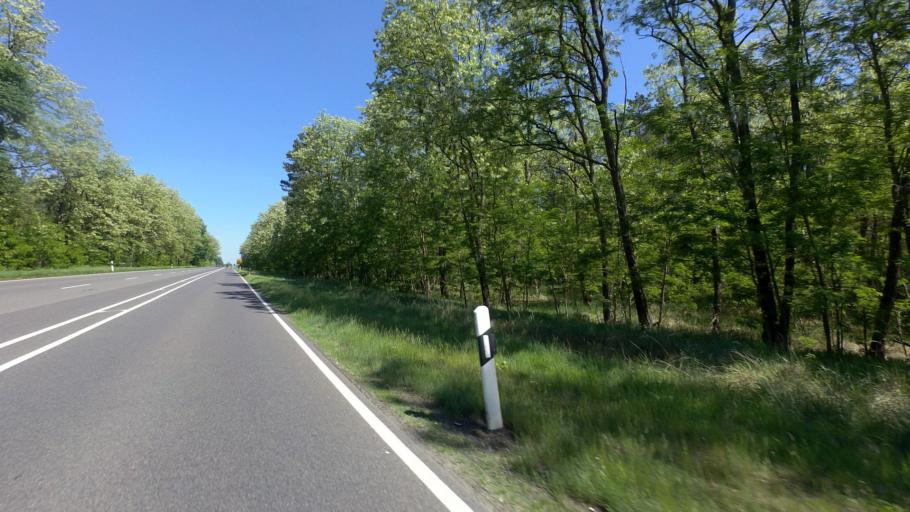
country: DE
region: Brandenburg
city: Spremberg
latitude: 51.6463
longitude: 14.3615
